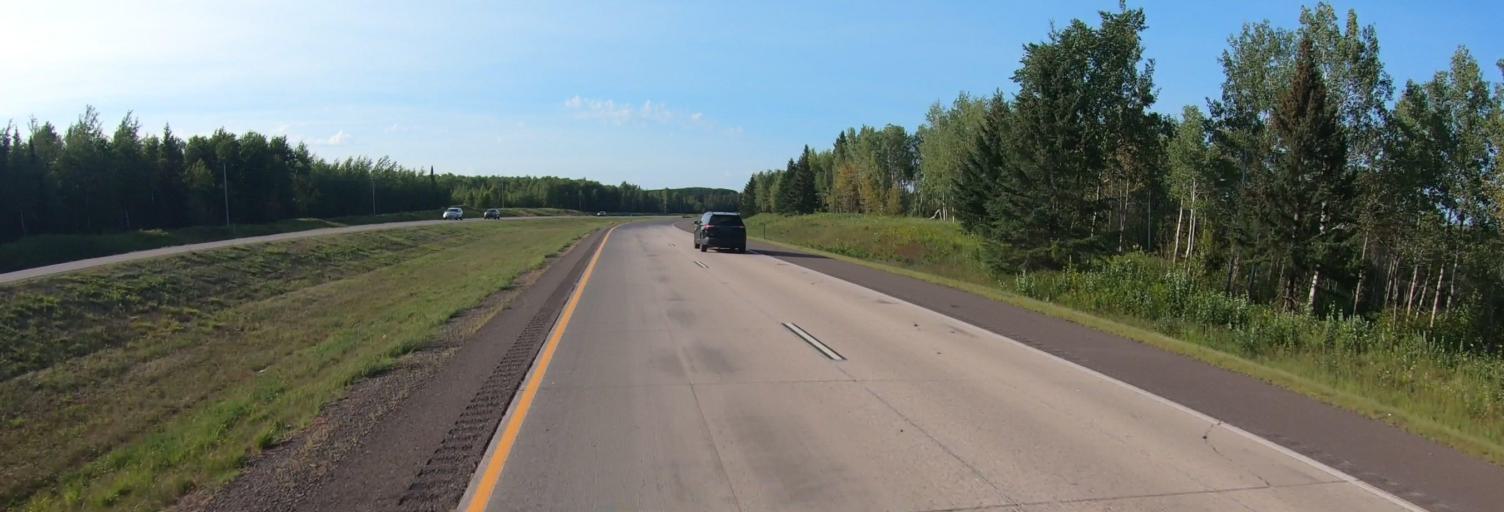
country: US
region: Minnesota
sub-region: Carlton County
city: Cloquet
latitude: 46.9755
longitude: -92.4687
